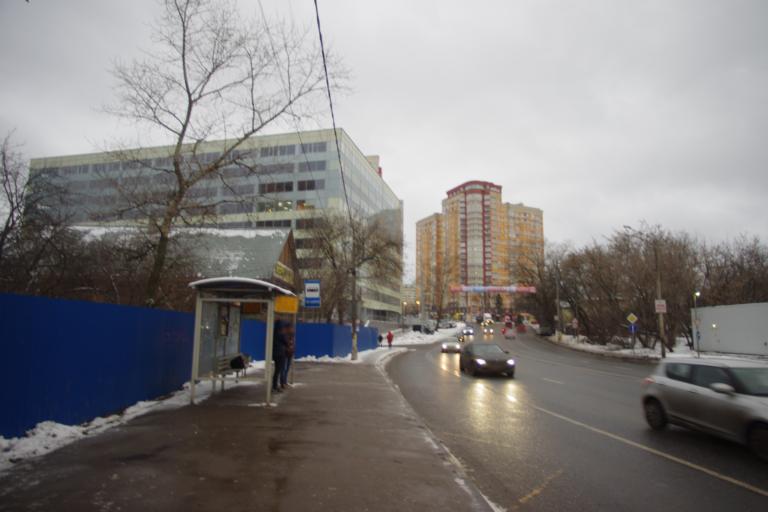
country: RU
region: Moskovskaya
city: Pavshino
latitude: 55.8158
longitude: 37.3548
